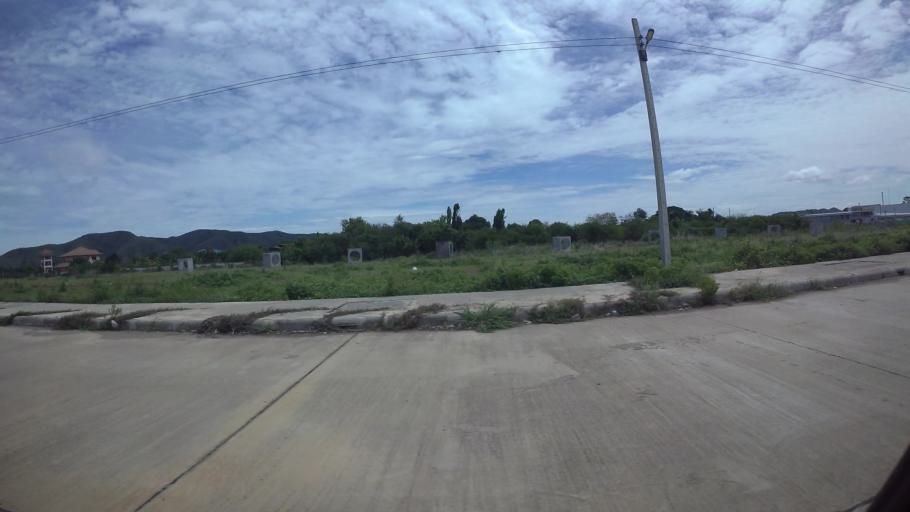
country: TH
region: Chon Buri
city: Sattahip
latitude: 12.6982
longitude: 100.8864
